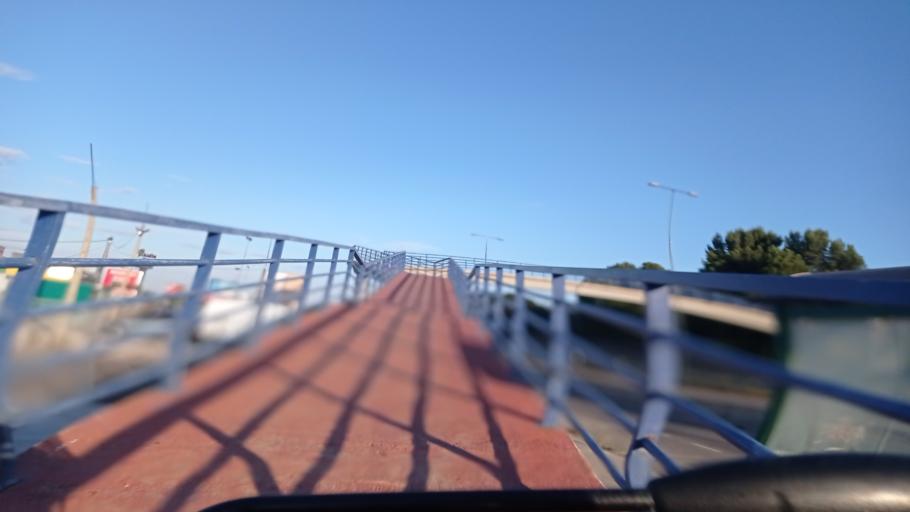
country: ES
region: Aragon
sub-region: Provincia de Zaragoza
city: Oliver-Valdefierro, Oliver, Valdefierro
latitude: 41.6768
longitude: -0.9578
